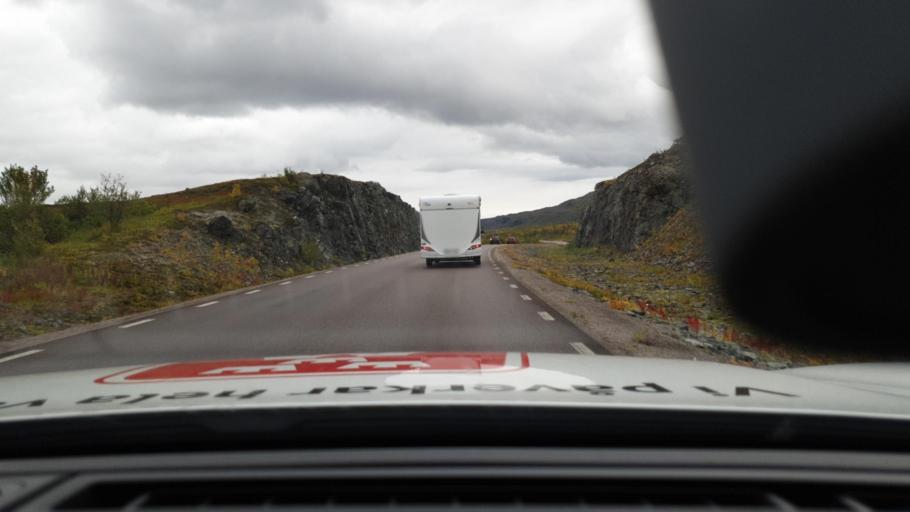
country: NO
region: Troms
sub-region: Bardu
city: Setermoen
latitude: 68.4301
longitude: 18.4609
